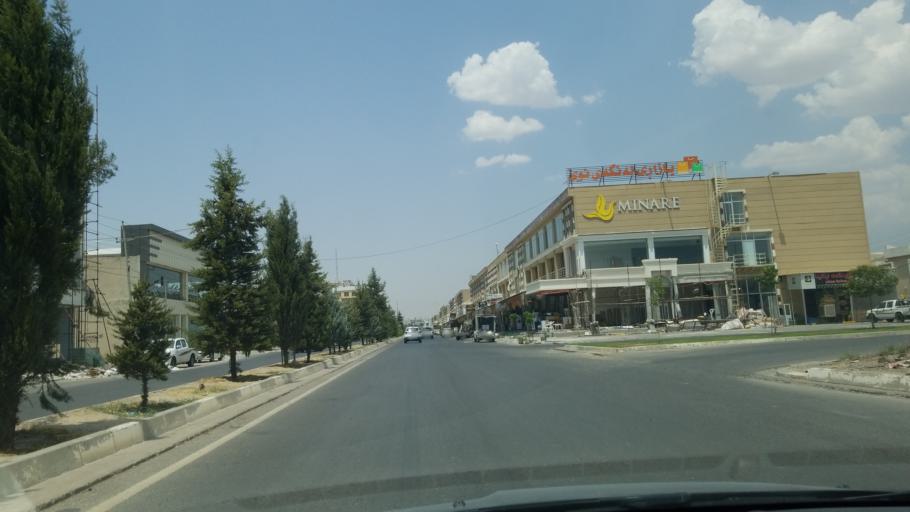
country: IQ
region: Arbil
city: Erbil
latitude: 36.1785
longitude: 44.0589
